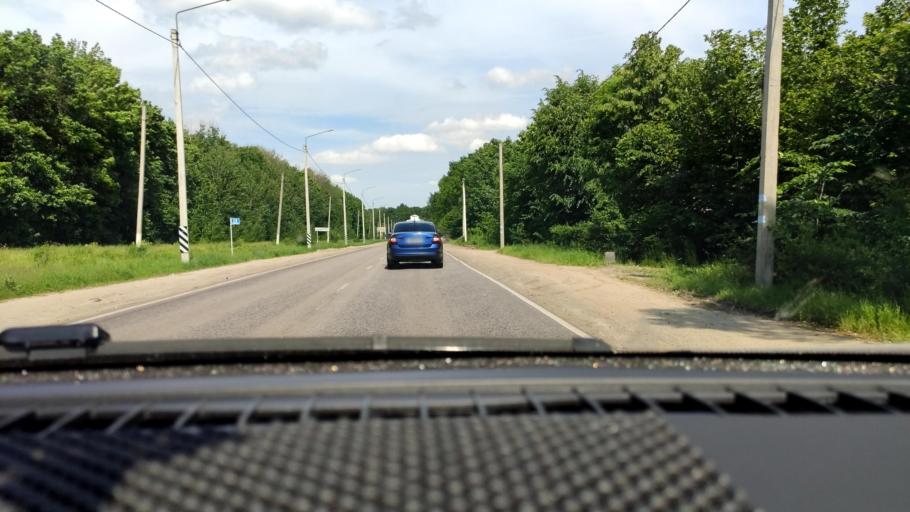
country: RU
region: Voronezj
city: Semiluki
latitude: 51.7392
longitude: 39.0478
